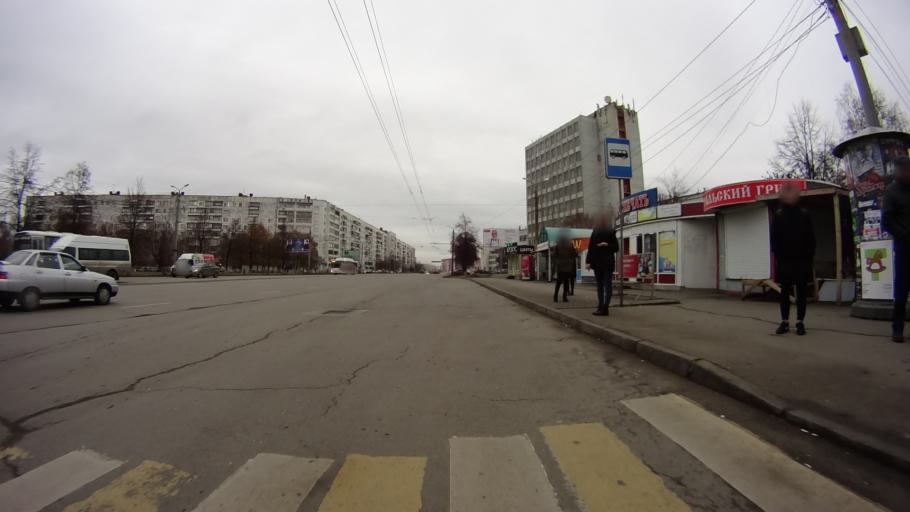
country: RU
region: Chelyabinsk
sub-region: Gorod Chelyabinsk
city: Chelyabinsk
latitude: 55.1942
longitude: 61.3543
